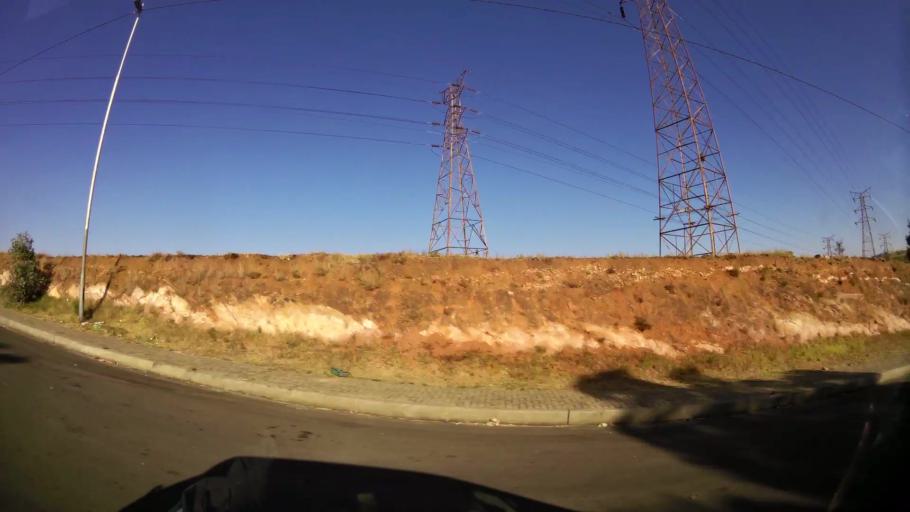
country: ZA
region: Gauteng
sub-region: City of Johannesburg Metropolitan Municipality
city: Johannesburg
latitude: -26.2168
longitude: 27.9827
